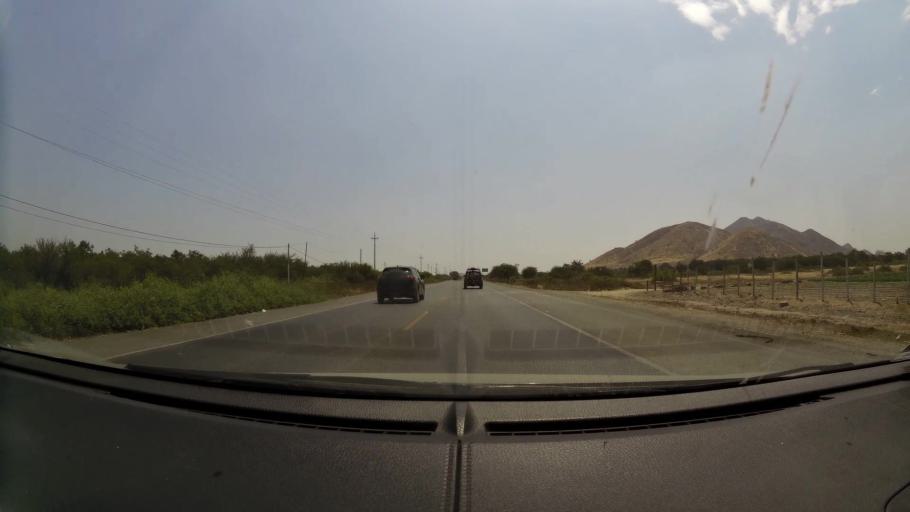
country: PE
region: La Libertad
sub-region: Chepen
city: Pacanga
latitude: -7.1160
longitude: -79.4915
